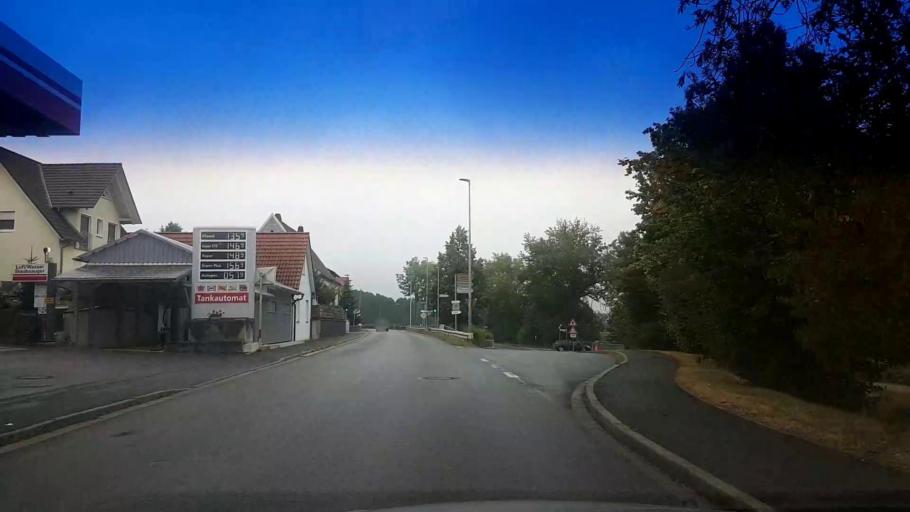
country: DE
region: Bavaria
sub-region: Upper Franconia
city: Heroldsbach
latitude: 49.6917
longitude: 11.0038
